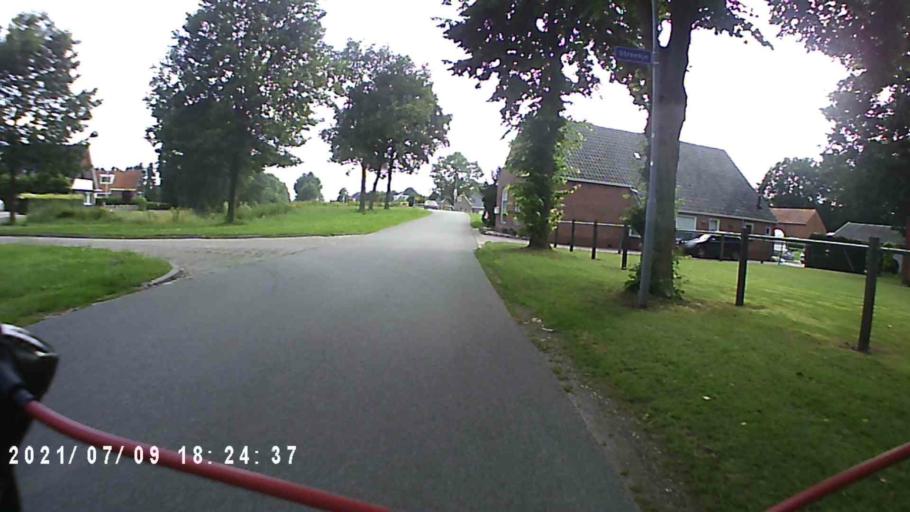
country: NL
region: Groningen
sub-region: Gemeente Pekela
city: Oude Pekela
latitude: 53.0502
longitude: 6.9912
